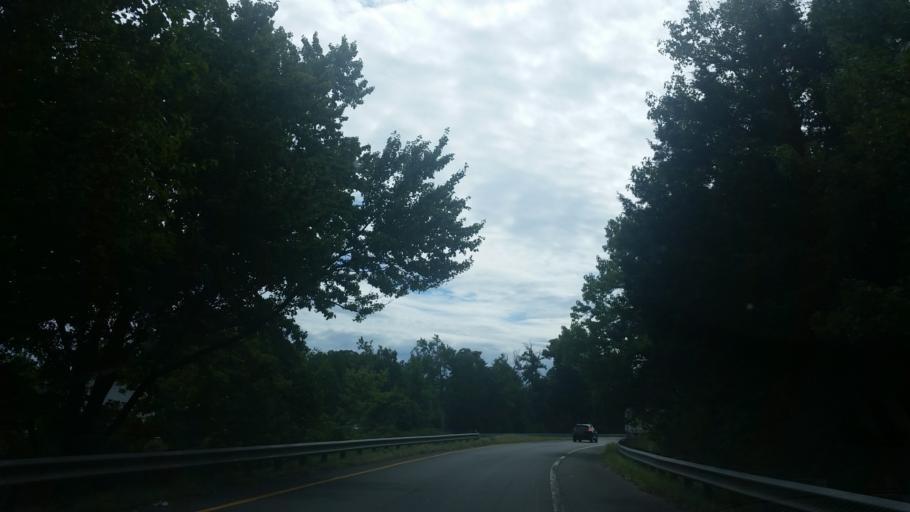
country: US
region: Virginia
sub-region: Stafford County
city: Falmouth
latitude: 38.3389
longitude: -77.4950
